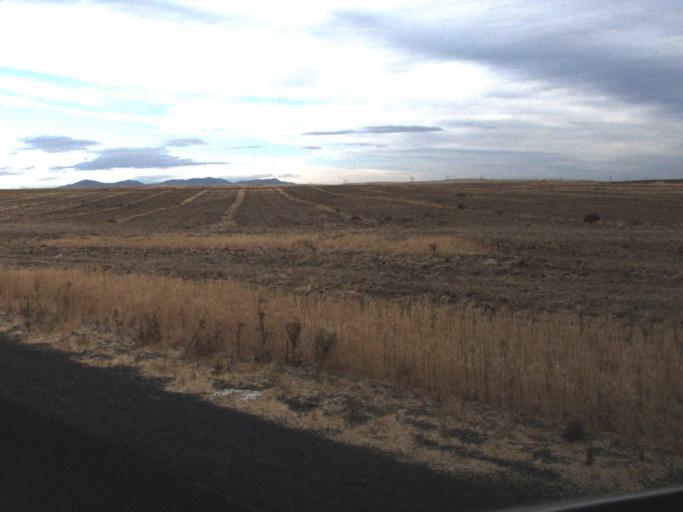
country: US
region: Washington
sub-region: Okanogan County
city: Coulee Dam
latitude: 47.7902
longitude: -118.7444
